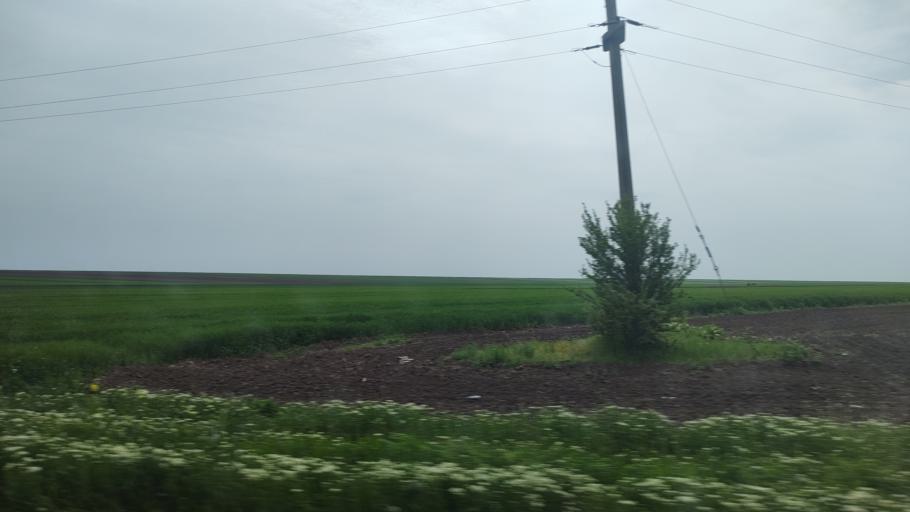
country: RO
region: Constanta
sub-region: Comuna Ciocarlia
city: Ciocarlia
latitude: 44.1064
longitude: 28.2989
